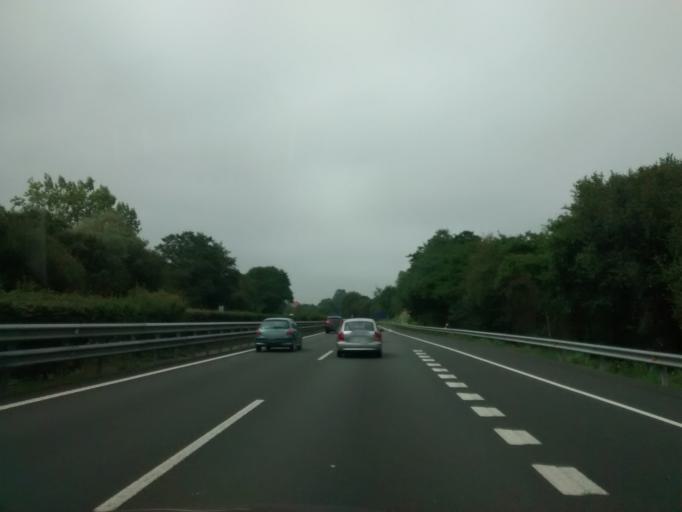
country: ES
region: Cantabria
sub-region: Provincia de Cantabria
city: Miengo
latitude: 43.4156
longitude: -3.9656
